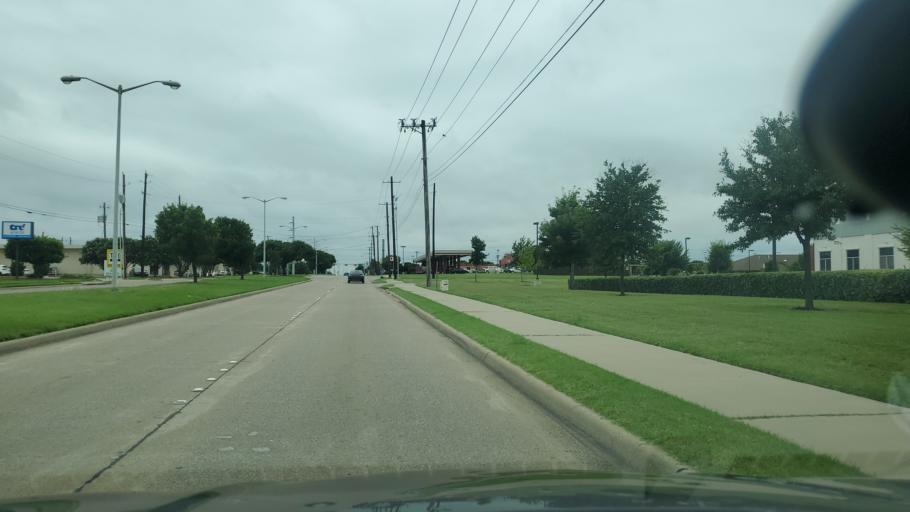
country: US
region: Texas
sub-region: Dallas County
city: Garland
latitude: 32.9472
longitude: -96.6654
